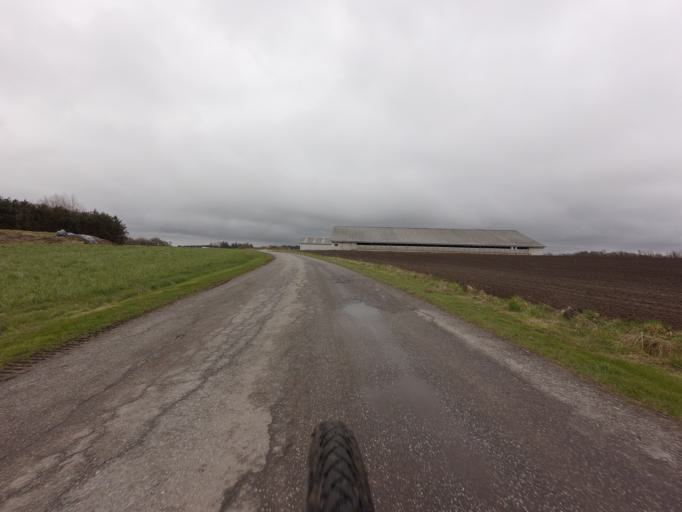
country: DK
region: North Denmark
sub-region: Jammerbugt Kommune
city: Pandrup
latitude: 57.3355
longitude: 9.7854
